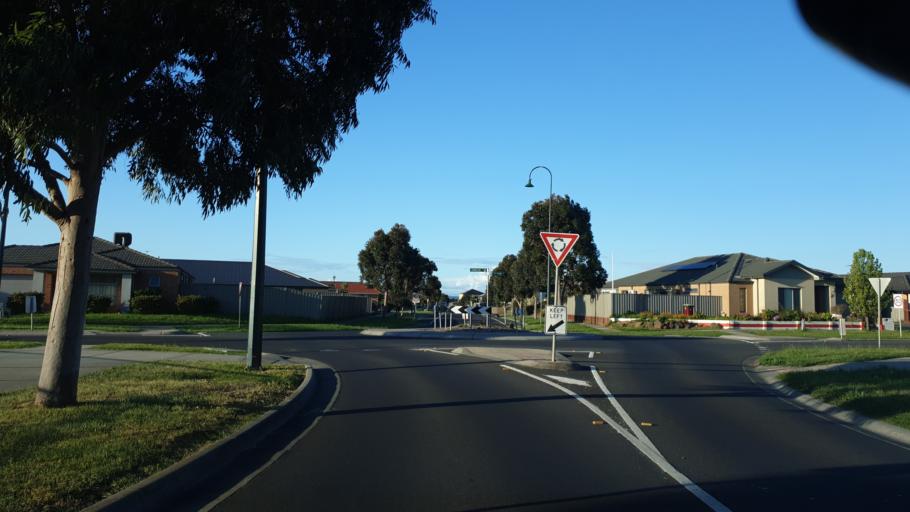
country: AU
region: Victoria
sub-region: Casey
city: Cranbourne East
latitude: -38.1036
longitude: 145.3069
